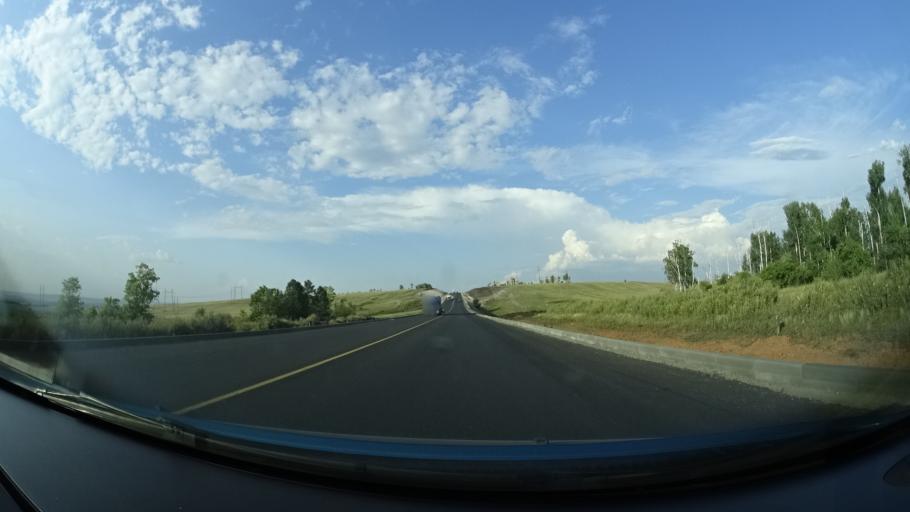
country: RU
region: Samara
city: Sukhodol
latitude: 53.7287
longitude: 50.8384
